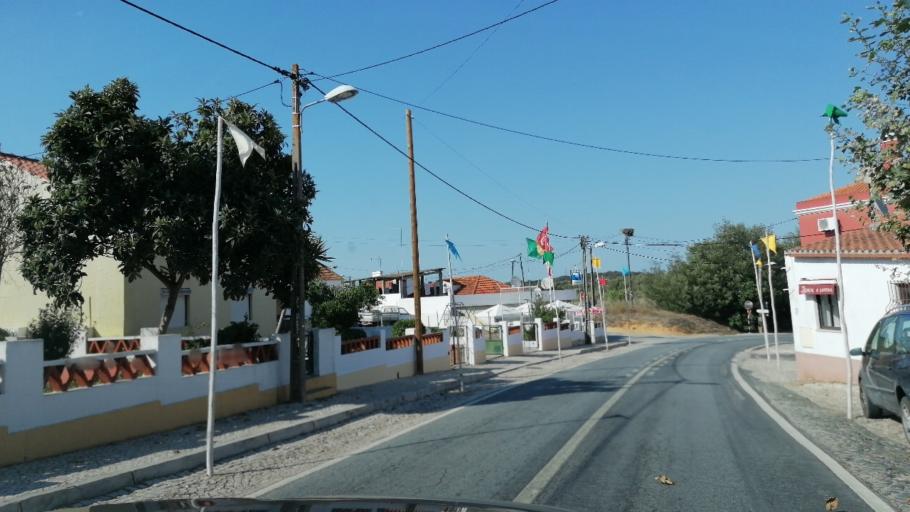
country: PT
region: Santarem
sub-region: Benavente
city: Poceirao
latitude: 38.7683
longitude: -8.6261
